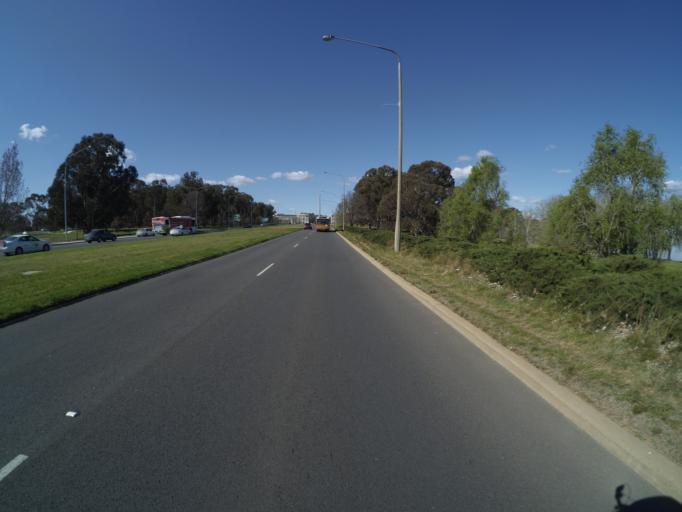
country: AU
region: Australian Capital Territory
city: Forrest
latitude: -35.3007
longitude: 149.1439
